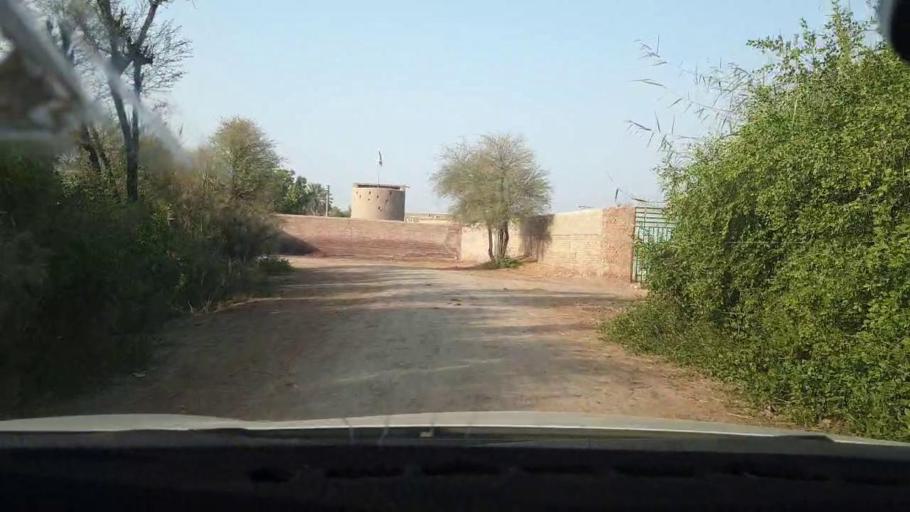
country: PK
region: Sindh
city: Berani
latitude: 25.8184
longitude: 68.7945
